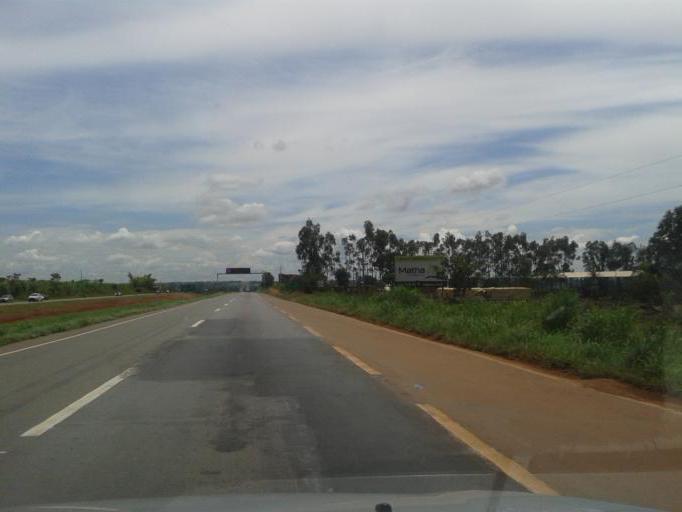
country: BR
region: Goias
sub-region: Aparecida De Goiania
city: Aparecida de Goiania
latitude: -16.8870
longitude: -49.2540
